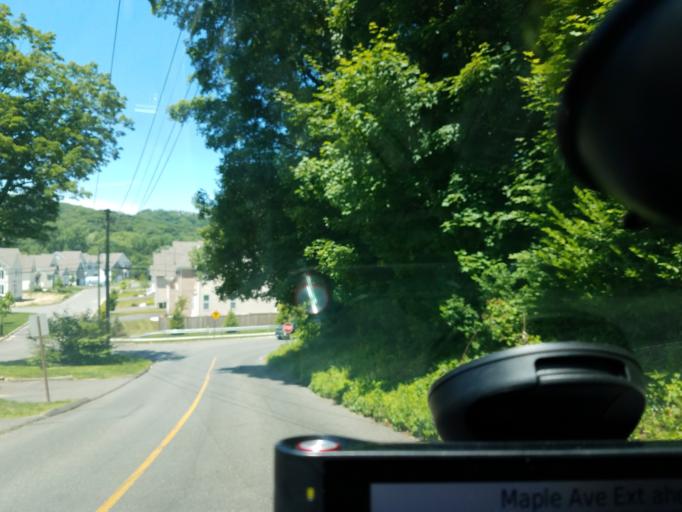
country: US
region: Connecticut
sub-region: Fairfield County
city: Bethel
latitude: 41.3794
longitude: -73.3988
